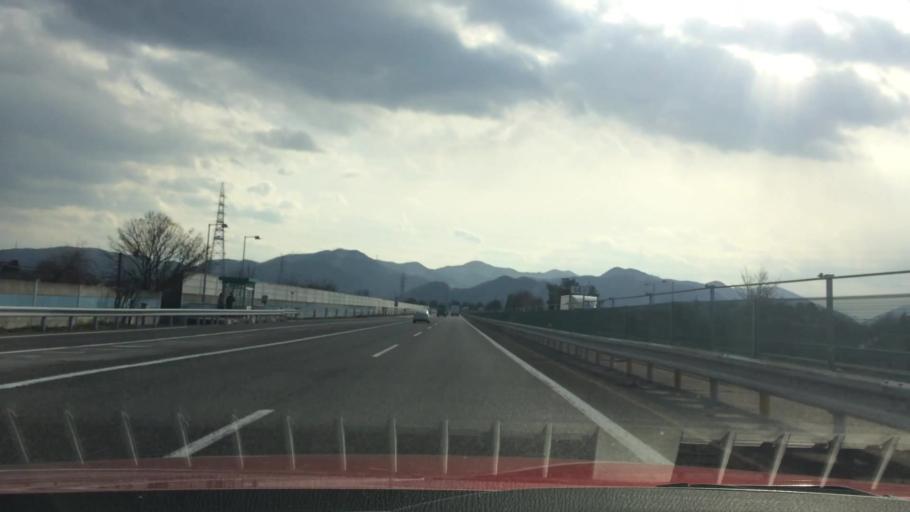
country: JP
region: Nagano
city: Shiojiri
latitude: 36.1457
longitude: 137.9677
